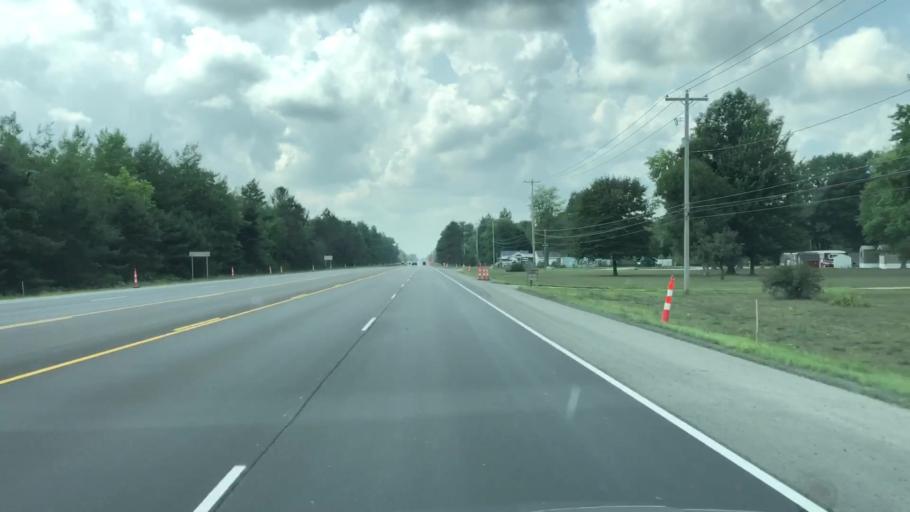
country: US
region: Michigan
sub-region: Isabella County
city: Shepherd
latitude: 43.6119
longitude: -84.6299
